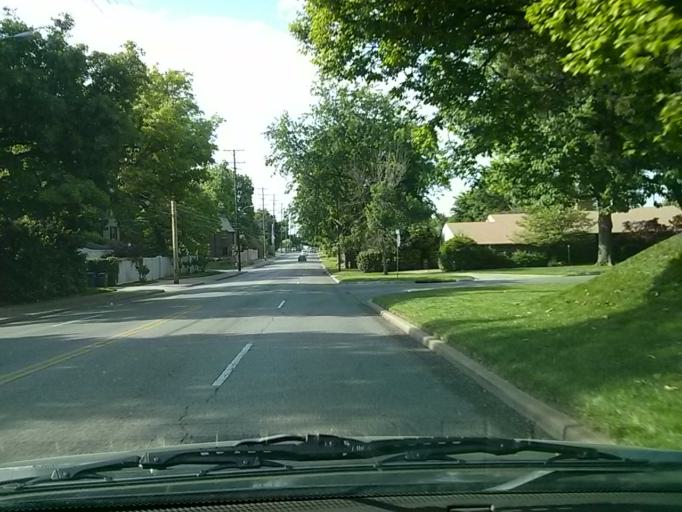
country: US
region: Oklahoma
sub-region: Tulsa County
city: Tulsa
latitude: 36.1266
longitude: -95.9757
